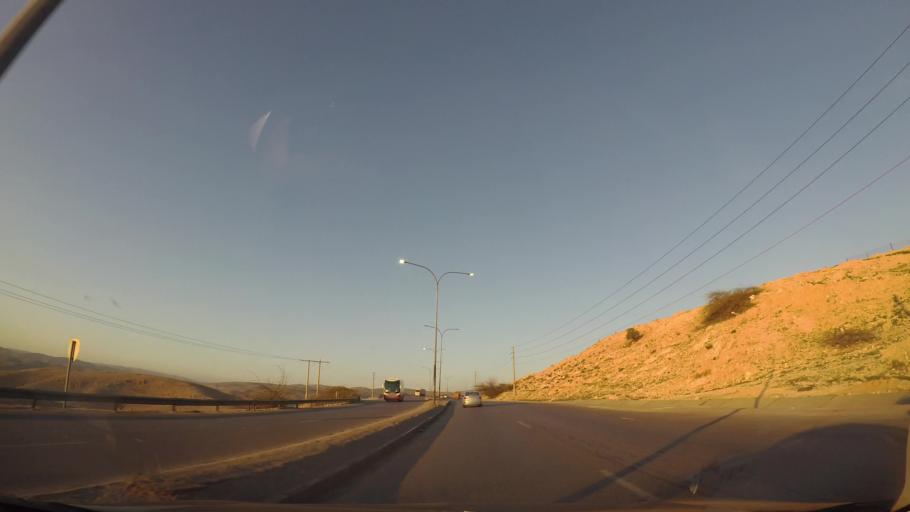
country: JO
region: Balqa
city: Yarqa
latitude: 31.8616
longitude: 35.7201
